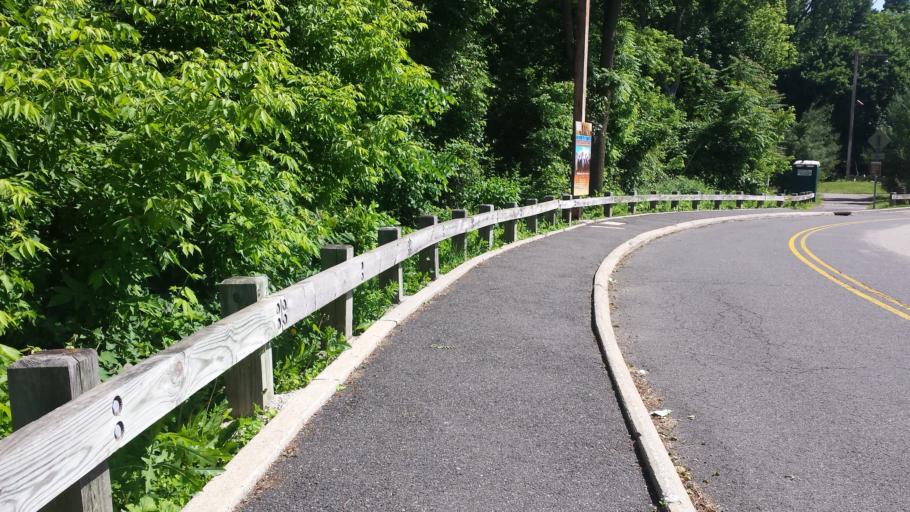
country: US
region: New York
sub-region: Westchester County
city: White Plains
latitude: 41.0371
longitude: -73.7774
